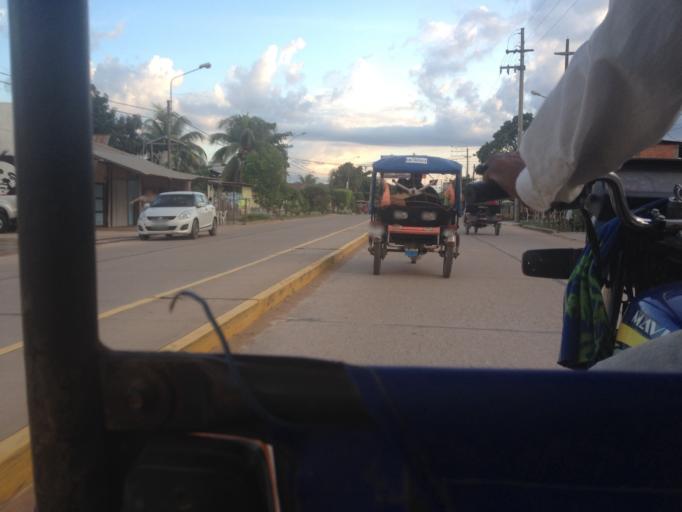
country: PE
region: Ucayali
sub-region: Provincia de Coronel Portillo
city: Pucallpa
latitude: -8.3810
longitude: -74.5692
